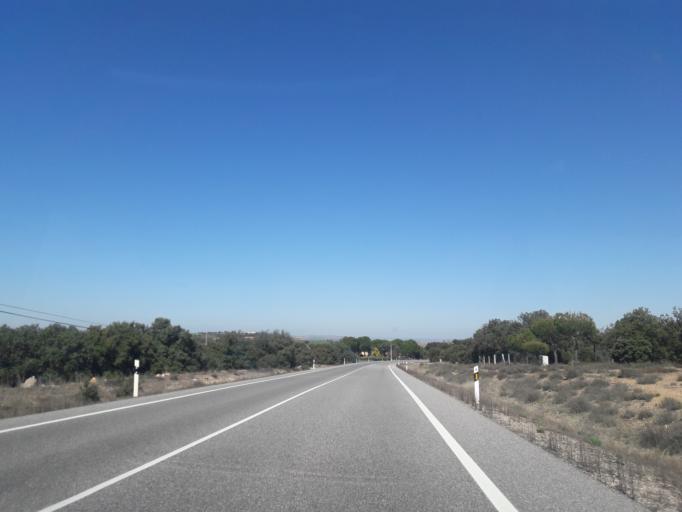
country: ES
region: Castille and Leon
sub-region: Provincia de Salamanca
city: Mozarbez
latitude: 40.8247
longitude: -5.6375
